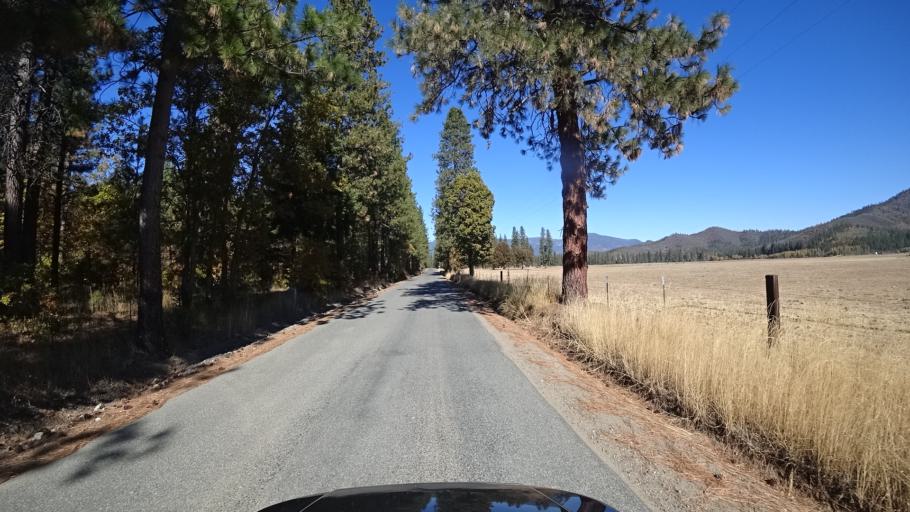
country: US
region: California
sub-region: Siskiyou County
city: Yreka
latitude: 41.5863
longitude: -122.9747
